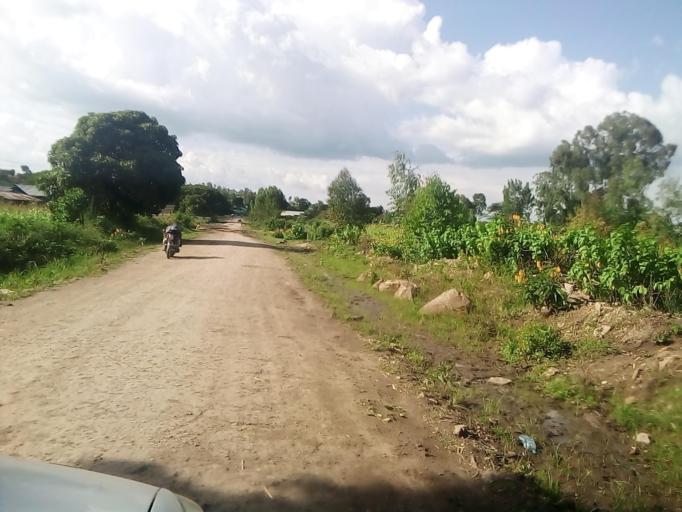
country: ET
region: Southern Nations, Nationalities, and People's Region
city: K'olito
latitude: 7.6630
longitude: 38.0473
